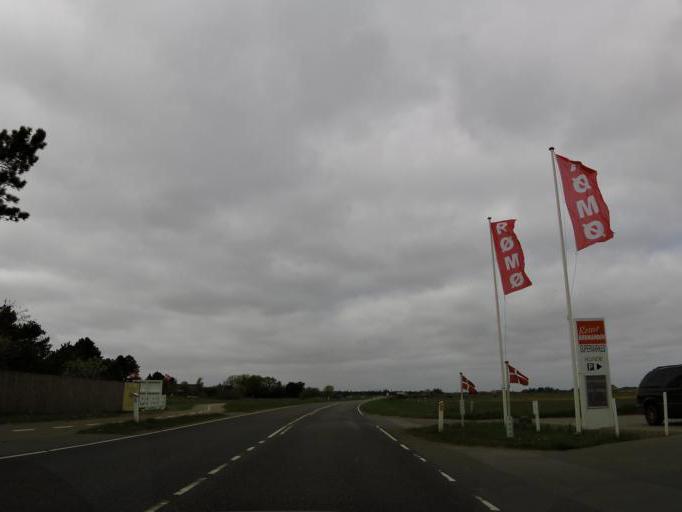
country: DE
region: Schleswig-Holstein
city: List
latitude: 55.1430
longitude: 8.5467
